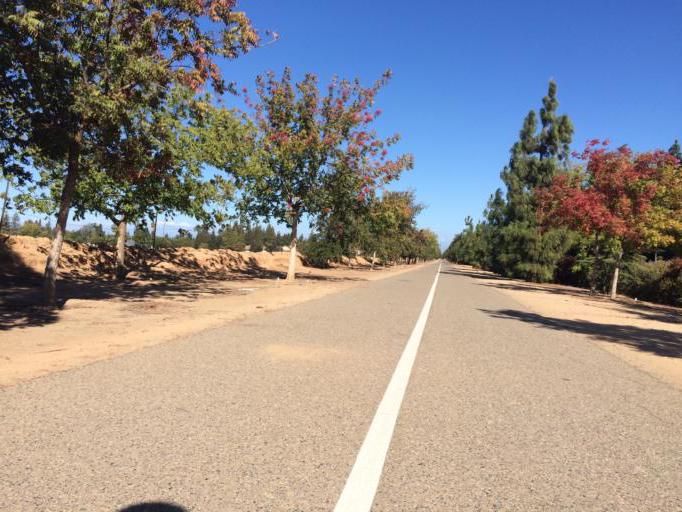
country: US
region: California
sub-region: Fresno County
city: Clovis
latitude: 36.8558
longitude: -119.7821
